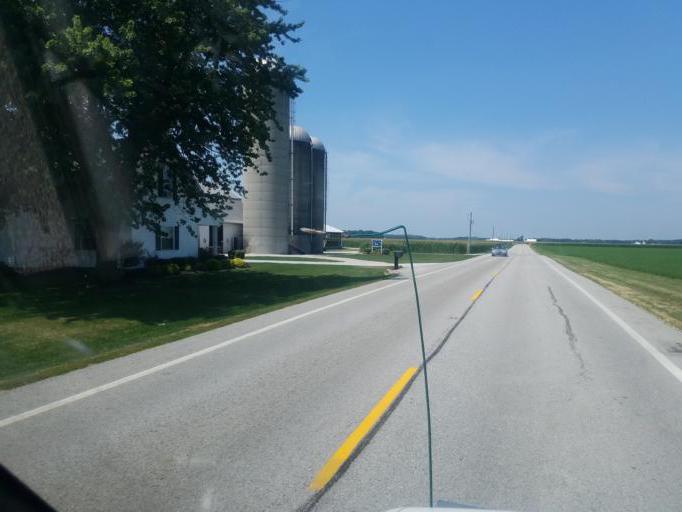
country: US
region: Ohio
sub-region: Auglaize County
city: New Bremen
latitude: 40.4589
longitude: -84.4341
